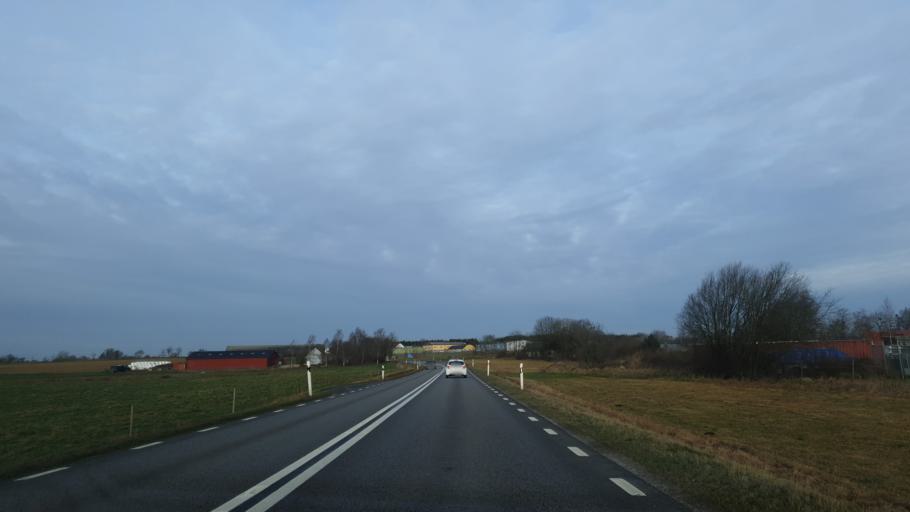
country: SE
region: Skane
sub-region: Horby Kommun
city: Hoerby
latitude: 55.7858
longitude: 13.6774
